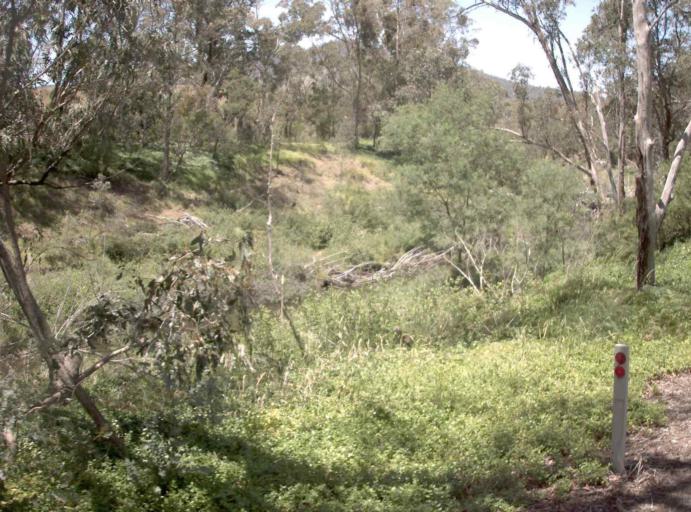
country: AU
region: Victoria
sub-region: East Gippsland
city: Bairnsdale
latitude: -37.4115
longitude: 147.8349
